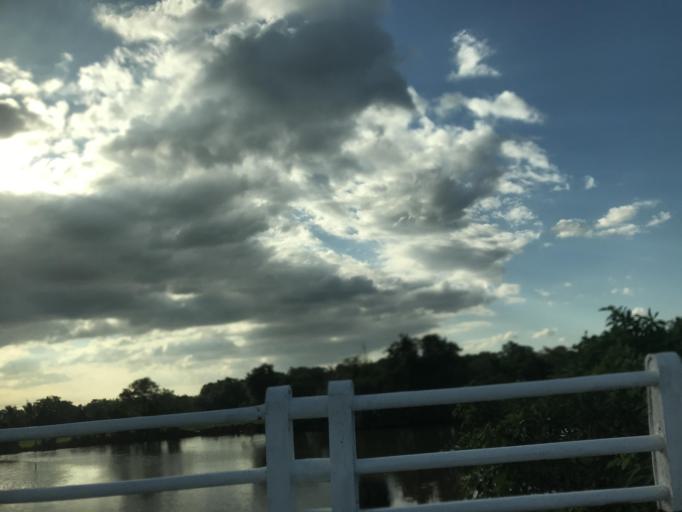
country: LK
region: Western
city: Gampaha
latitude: 7.0970
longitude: 79.9911
